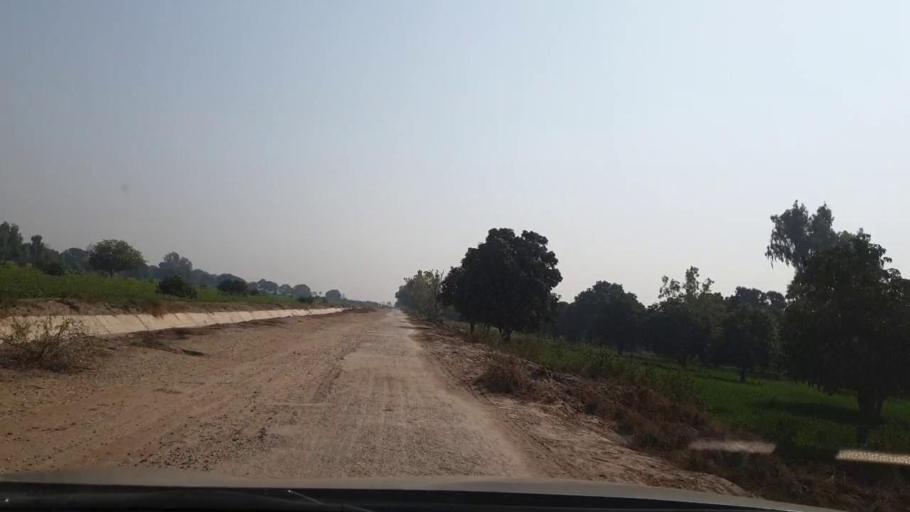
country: PK
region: Sindh
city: Tando Allahyar
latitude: 25.5200
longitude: 68.7814
